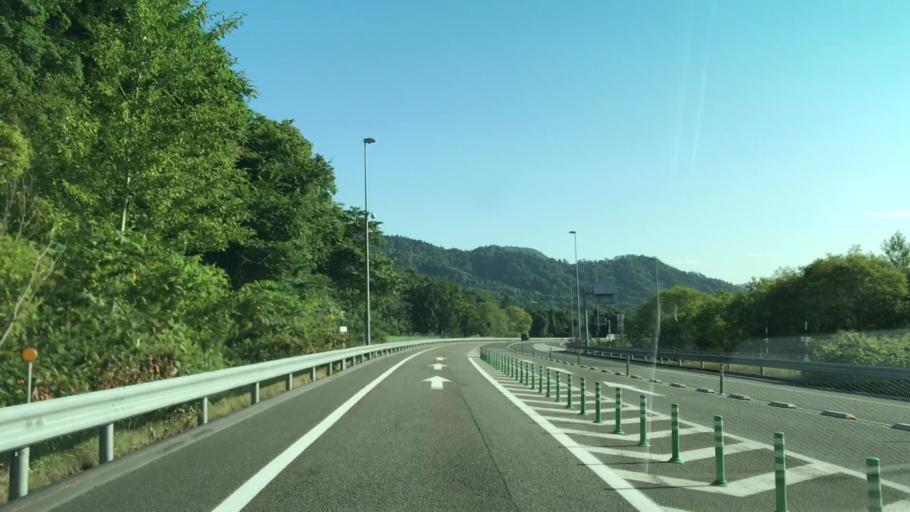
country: JP
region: Hokkaido
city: Iwamizawa
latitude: 42.9202
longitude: 142.0364
